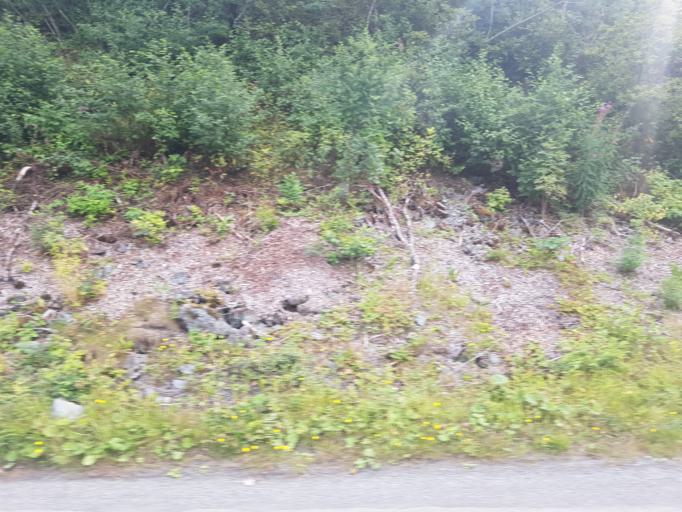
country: NO
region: Sor-Trondelag
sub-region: Trondheim
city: Trondheim
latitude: 63.3832
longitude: 10.3711
